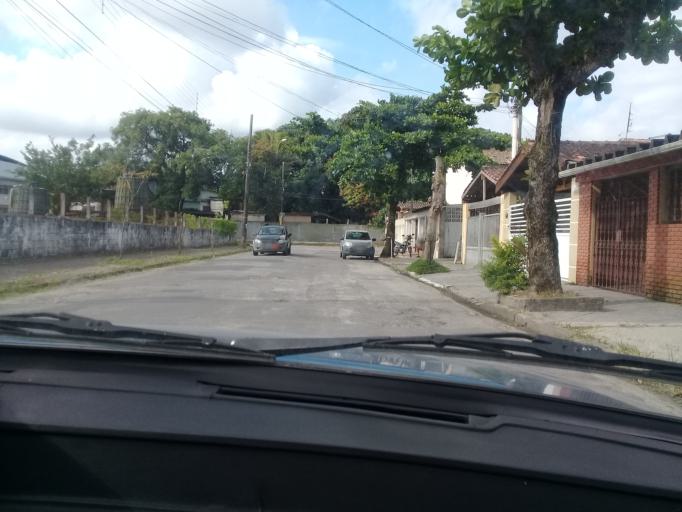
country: BR
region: Sao Paulo
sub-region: Guaruja
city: Guaruja
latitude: -23.9879
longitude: -46.2792
